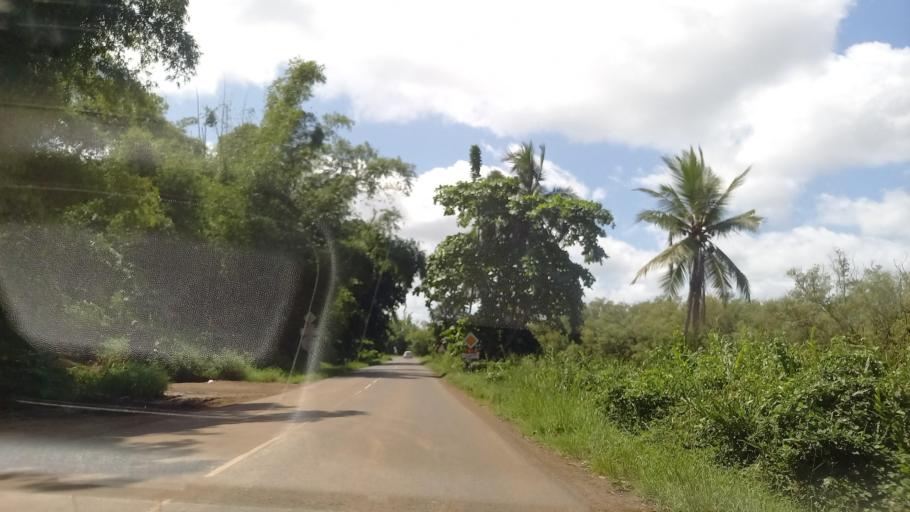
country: YT
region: Bandraboua
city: Bandraboua
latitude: -12.7226
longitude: 45.1284
